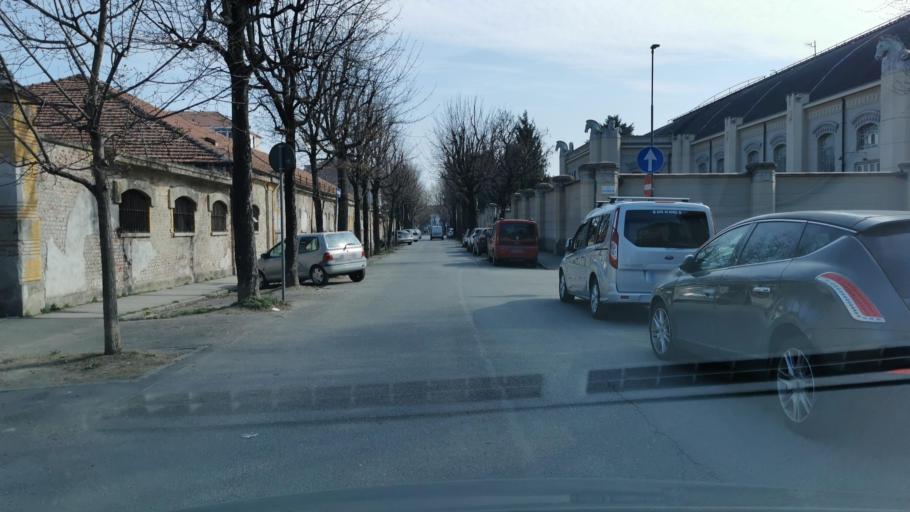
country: IT
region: Piedmont
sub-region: Provincia di Torino
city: Pinerolo
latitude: 44.8895
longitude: 7.3343
